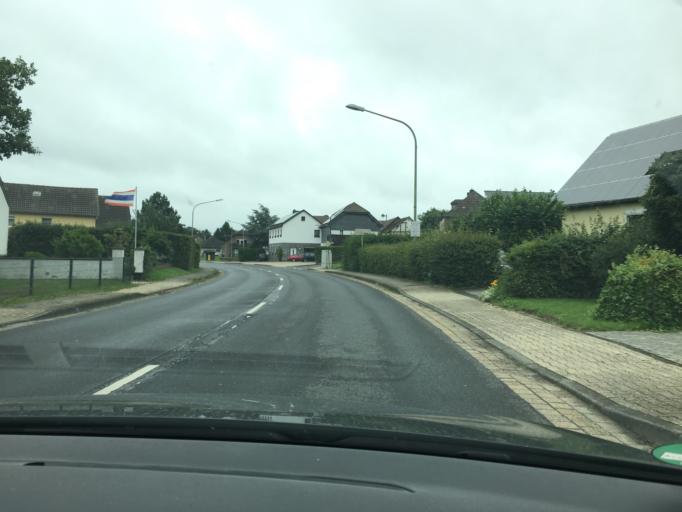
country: DE
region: North Rhine-Westphalia
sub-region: Regierungsbezirk Koln
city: Hurtgenwald
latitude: 50.7257
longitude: 6.3934
